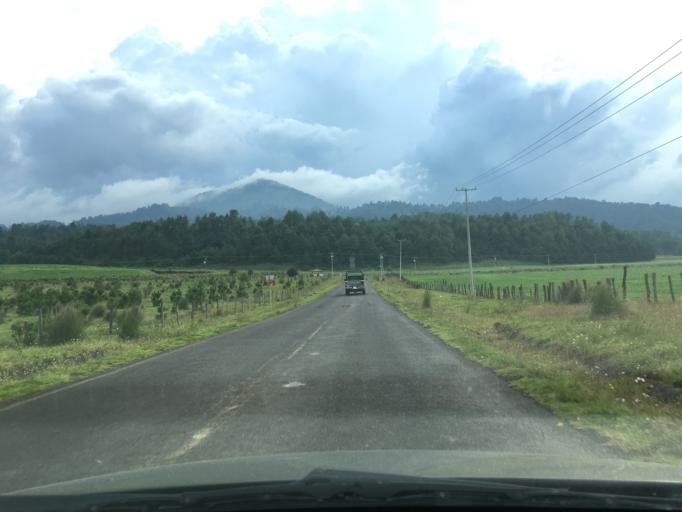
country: MX
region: Michoacan
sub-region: Nahuatzen
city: Sevina
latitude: 19.6141
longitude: -101.8575
